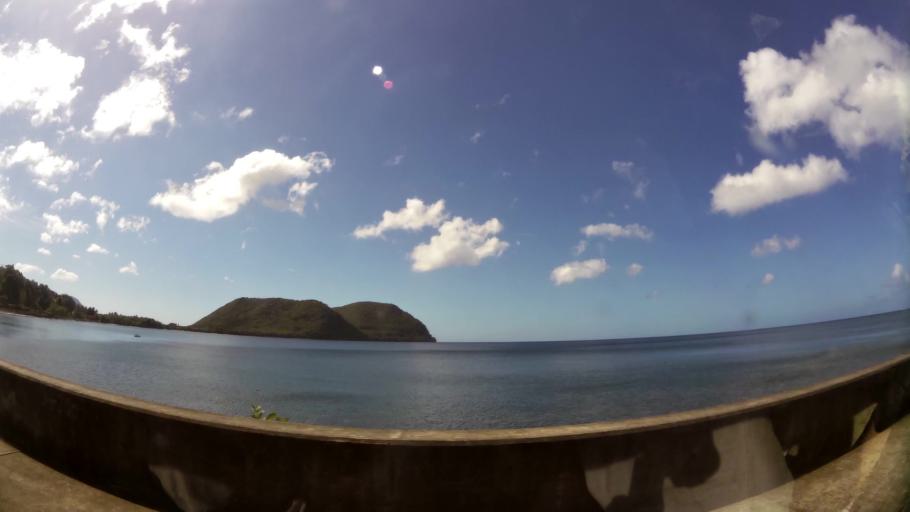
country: DM
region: Saint John
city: Portsmouth
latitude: 15.6006
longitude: -61.4623
